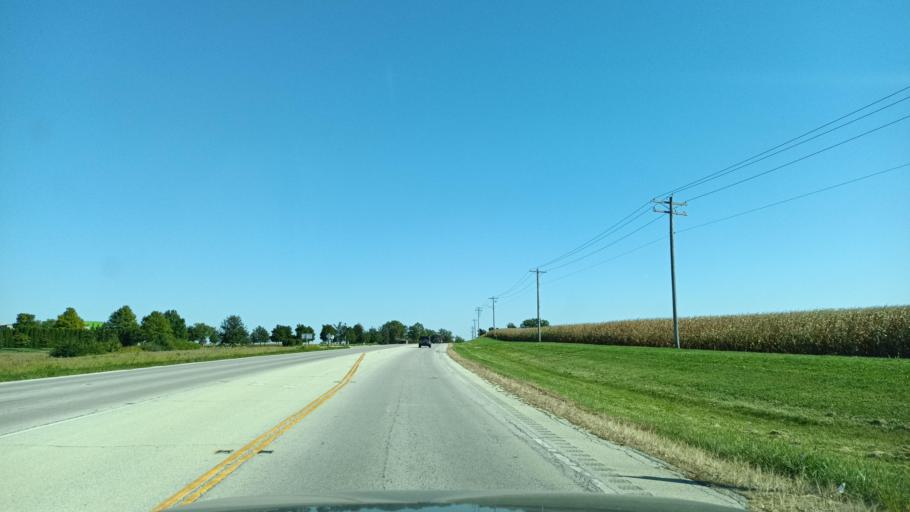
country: US
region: Illinois
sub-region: Champaign County
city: Lake of the Woods
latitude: 40.1841
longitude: -88.3646
